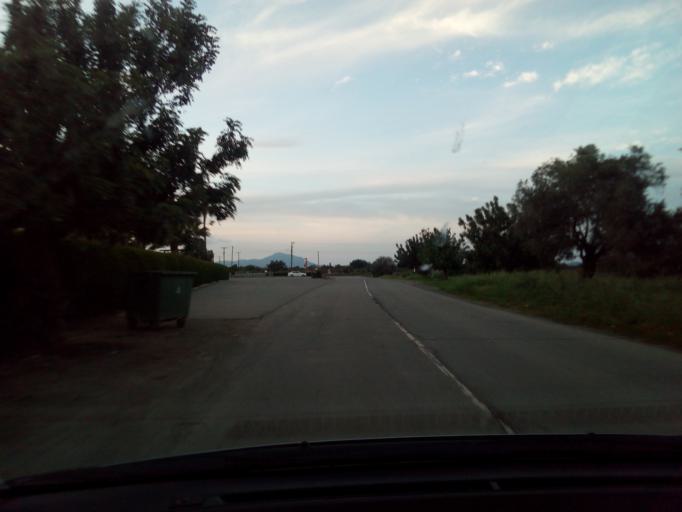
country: CY
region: Larnaka
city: Tersefanou
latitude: 34.8001
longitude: 33.5081
